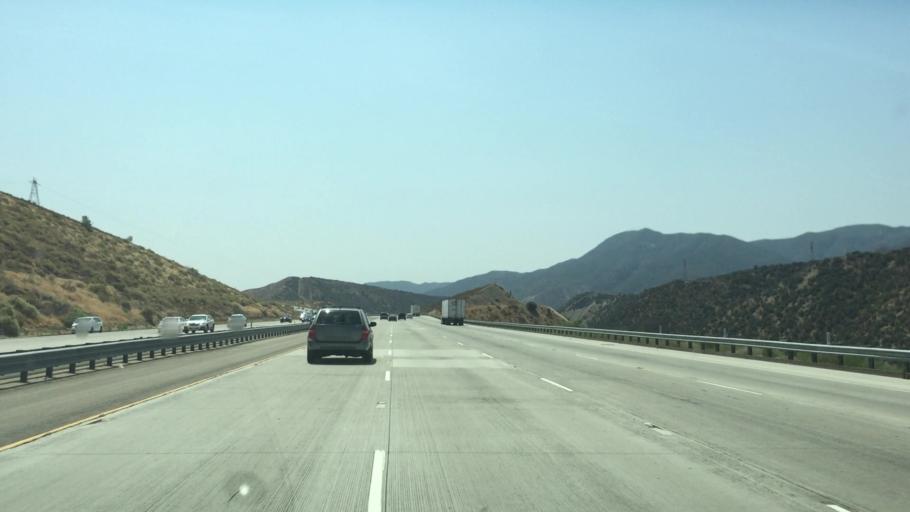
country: US
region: California
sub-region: Kern County
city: Lebec
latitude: 34.6922
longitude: -118.7892
